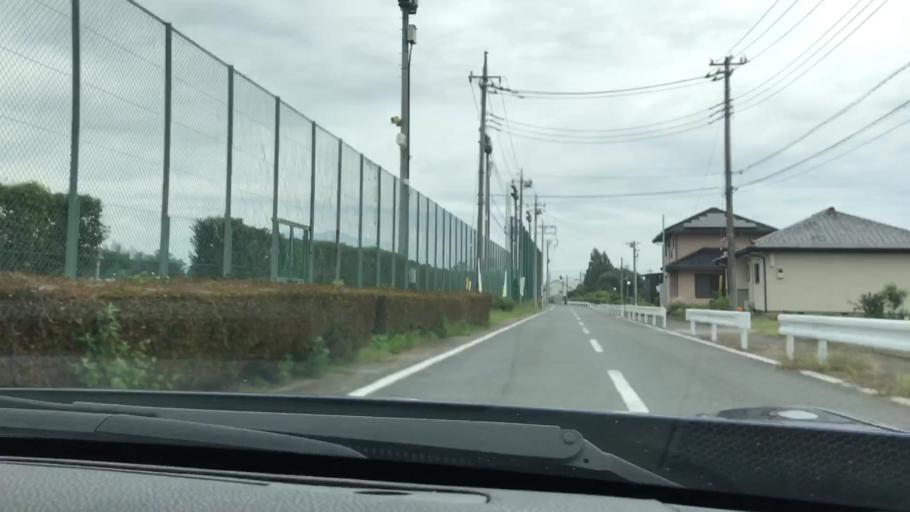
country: JP
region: Gunma
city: Kanekomachi
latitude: 36.4006
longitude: 138.9900
